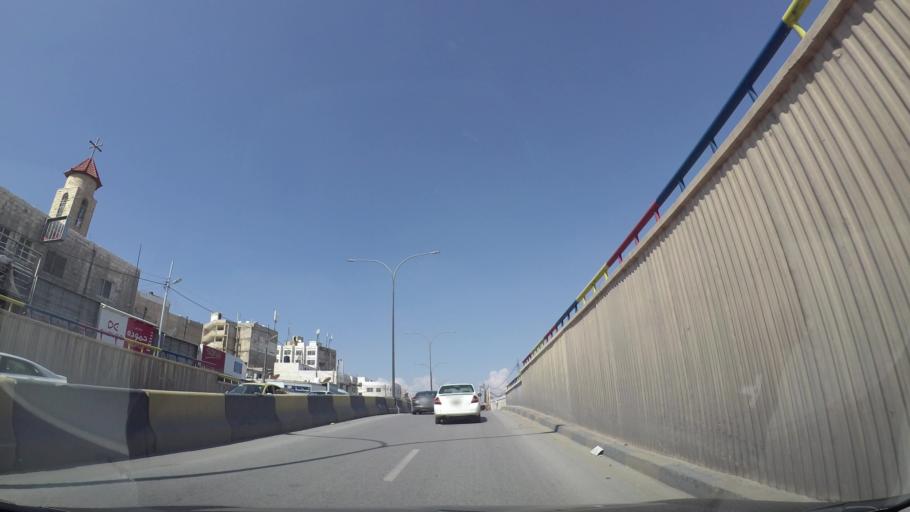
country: JO
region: Zarqa
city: Zarqa
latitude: 32.0616
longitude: 36.0943
